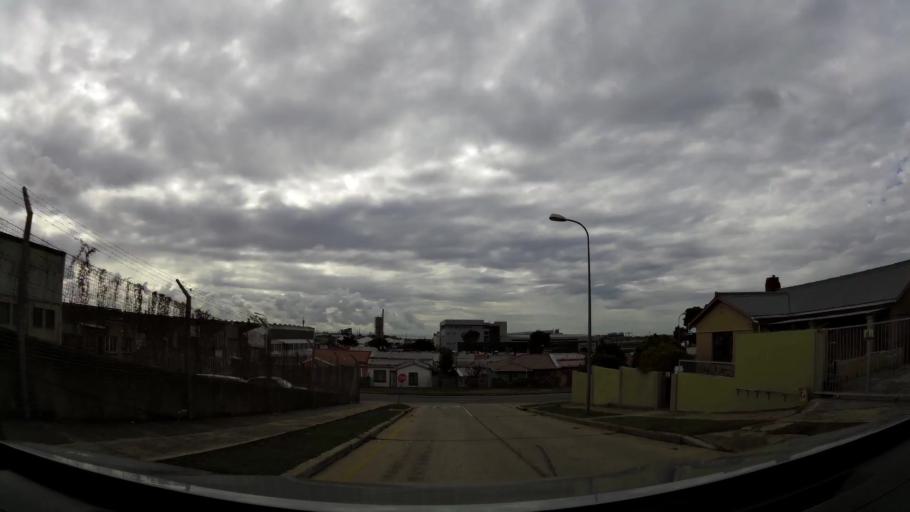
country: ZA
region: Eastern Cape
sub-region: Nelson Mandela Bay Metropolitan Municipality
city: Port Elizabeth
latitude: -33.9375
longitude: 25.5852
